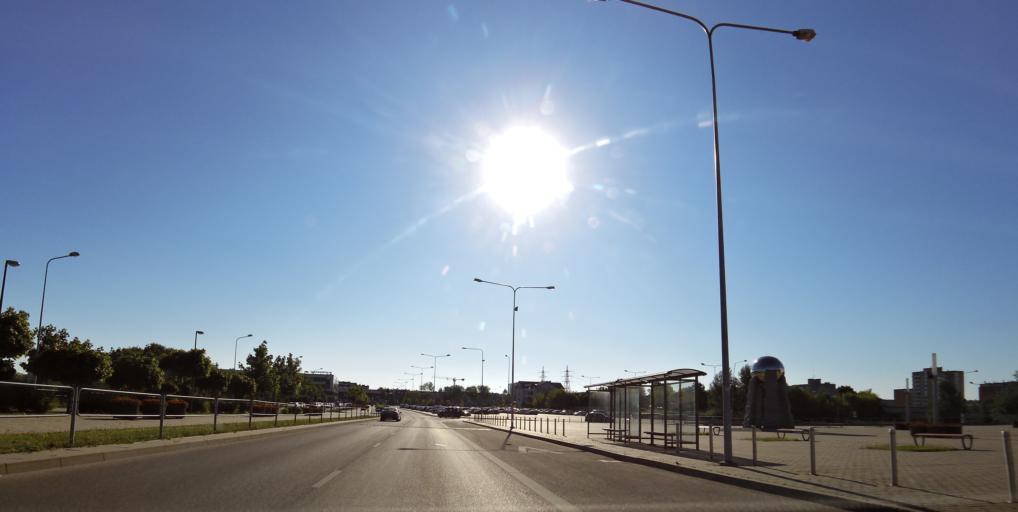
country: LT
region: Vilnius County
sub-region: Vilnius
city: Vilnius
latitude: 54.7171
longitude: 25.2806
